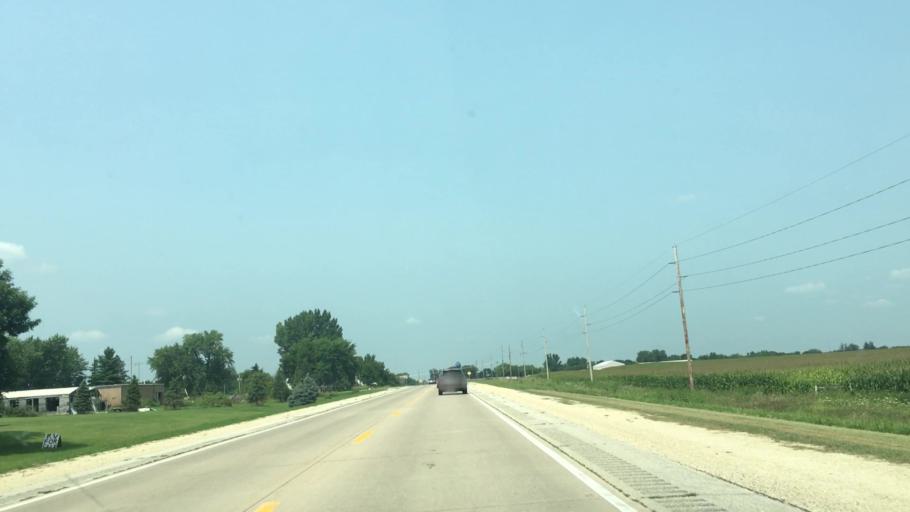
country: US
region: Iowa
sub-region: Fayette County
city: Oelwein
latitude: 42.6061
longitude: -91.9031
